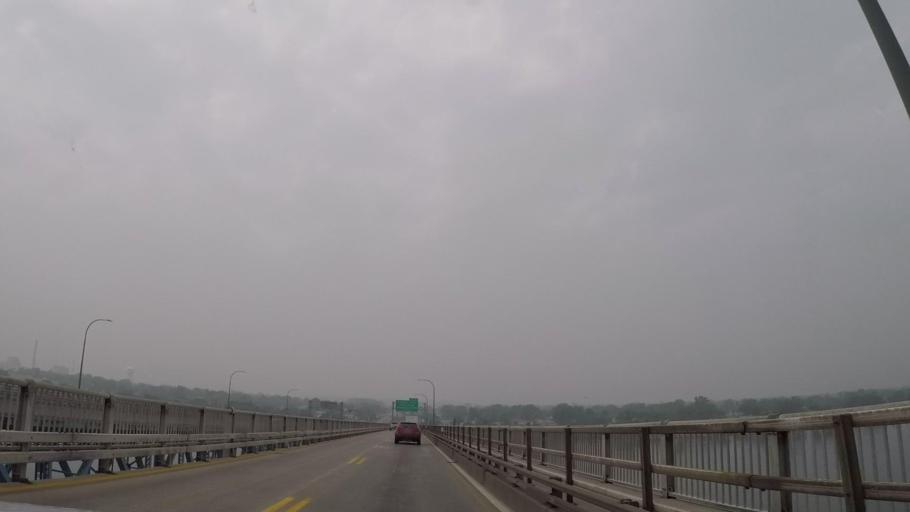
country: US
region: New York
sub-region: Niagara County
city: Niagara Falls
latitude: 43.0705
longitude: -78.9906
